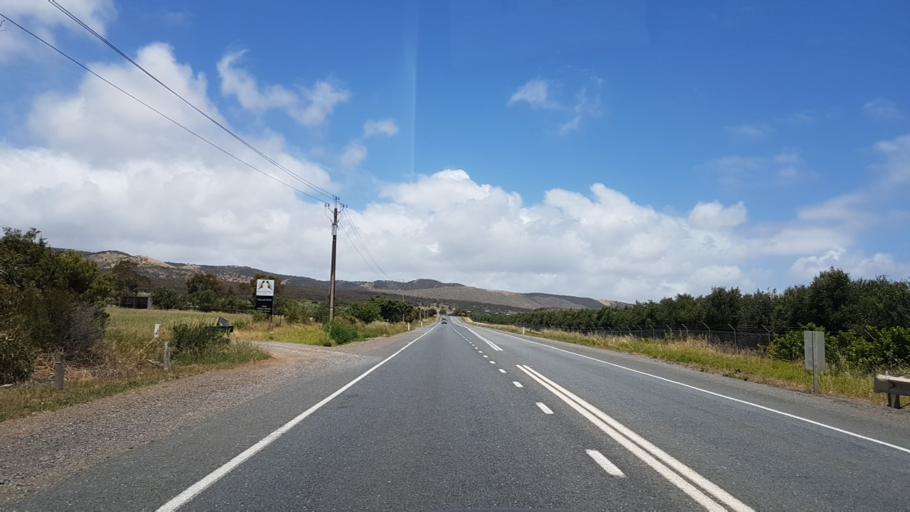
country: AU
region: South Australia
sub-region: Onkaparinga
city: Aldinga
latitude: -35.3133
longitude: 138.4737
